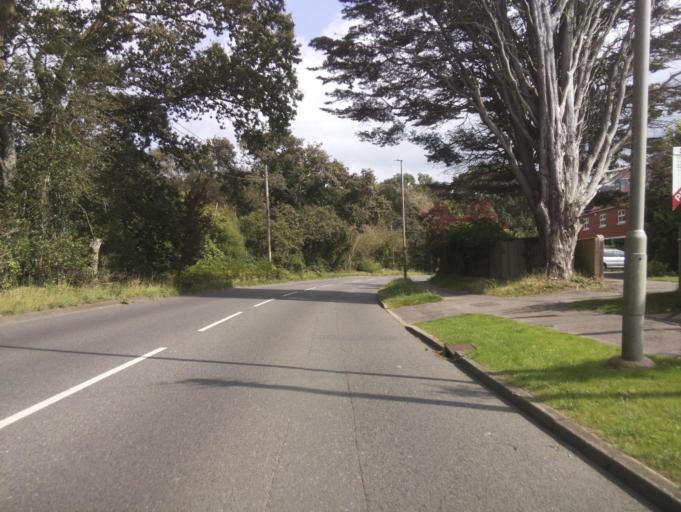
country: GB
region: England
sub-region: Hampshire
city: New Milton
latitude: 50.7479
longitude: -1.6906
